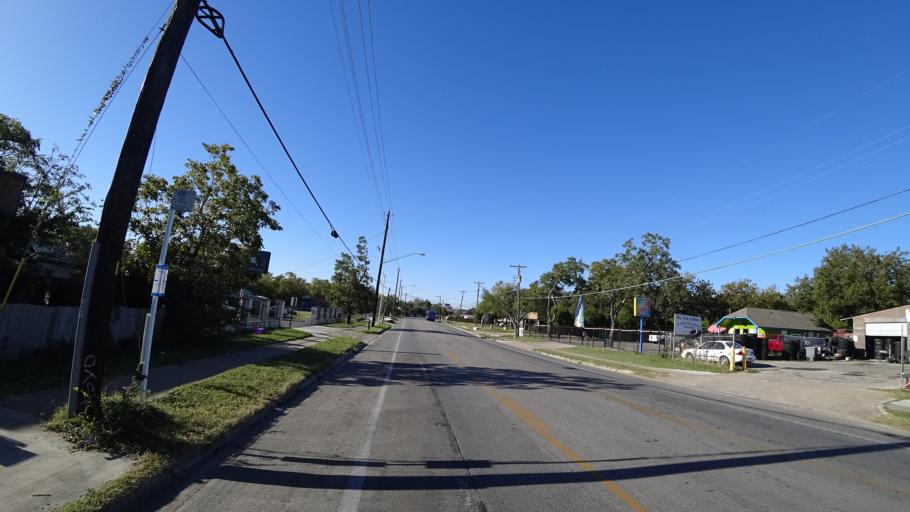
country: US
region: Texas
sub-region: Travis County
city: Austin
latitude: 30.3063
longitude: -97.6801
